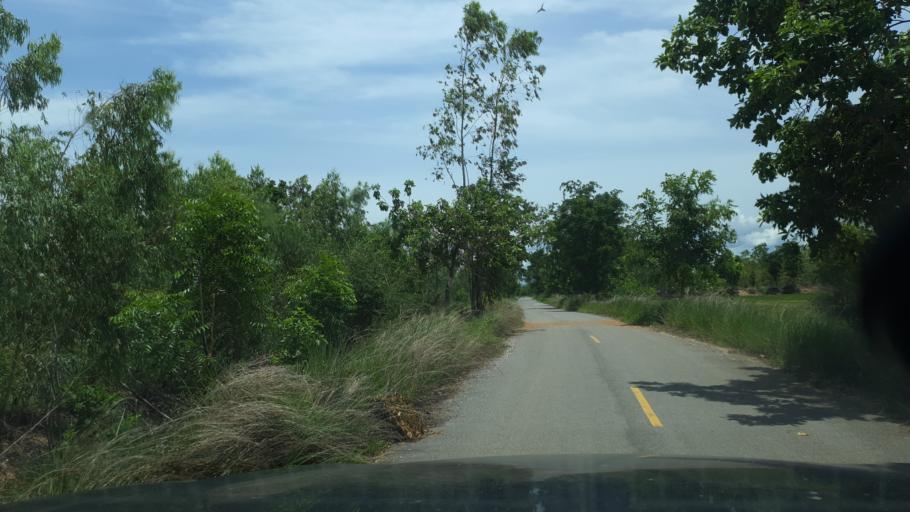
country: TH
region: Sukhothai
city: Ban Na
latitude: 17.1204
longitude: 99.6752
